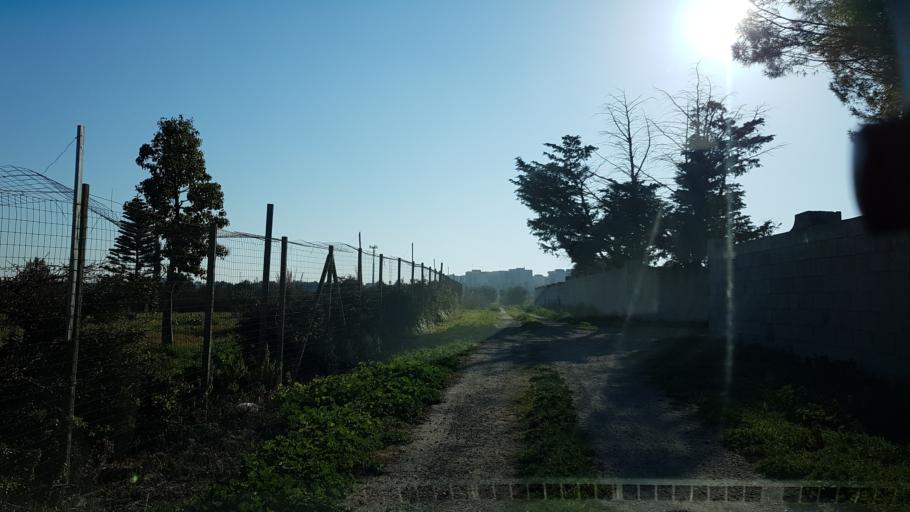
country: IT
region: Apulia
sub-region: Provincia di Brindisi
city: Brindisi
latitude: 40.6523
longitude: 17.9286
